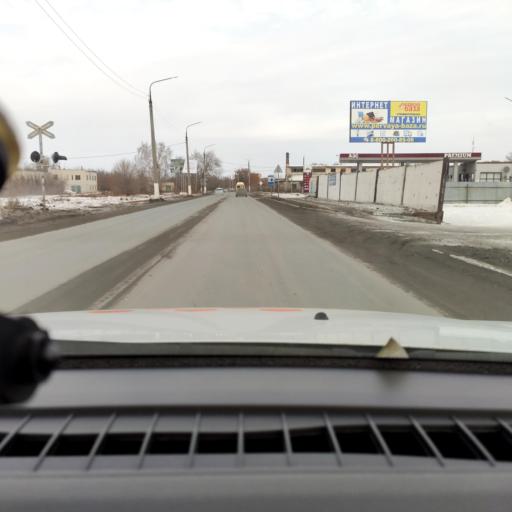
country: RU
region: Samara
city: Chapayevsk
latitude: 52.9648
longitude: 49.6928
